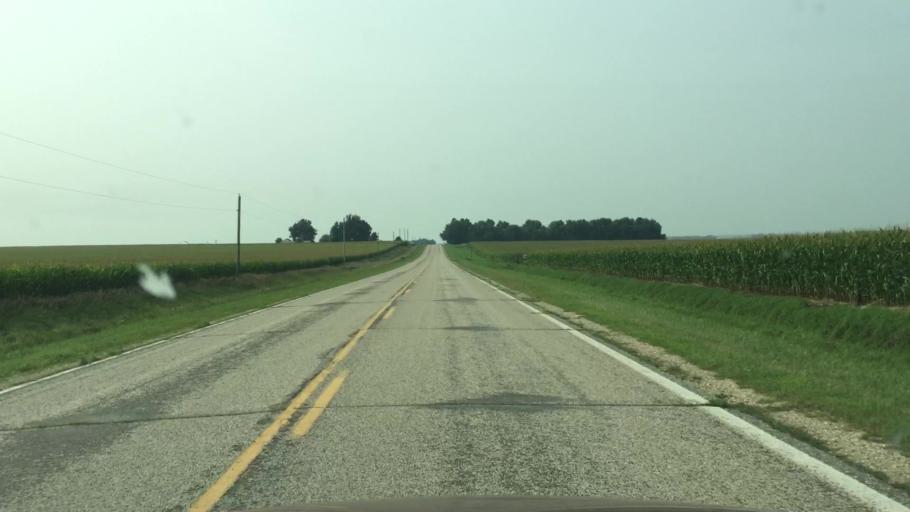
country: US
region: Iowa
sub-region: O'Brien County
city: Sheldon
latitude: 43.2688
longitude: -95.7830
